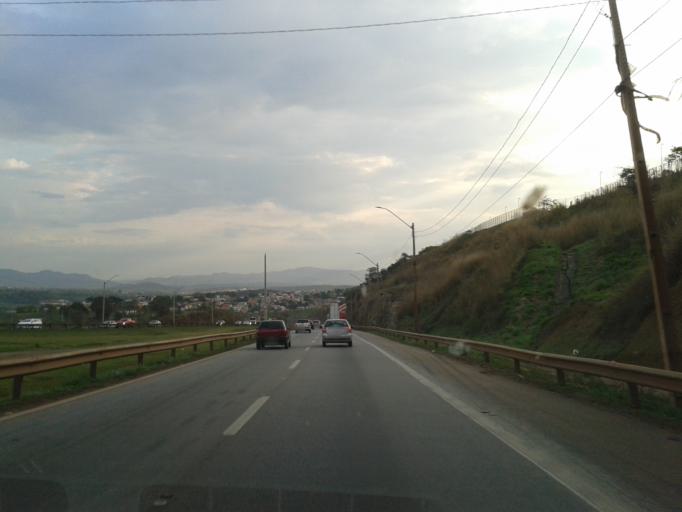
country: BR
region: Minas Gerais
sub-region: Betim
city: Betim
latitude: -19.9620
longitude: -44.1567
